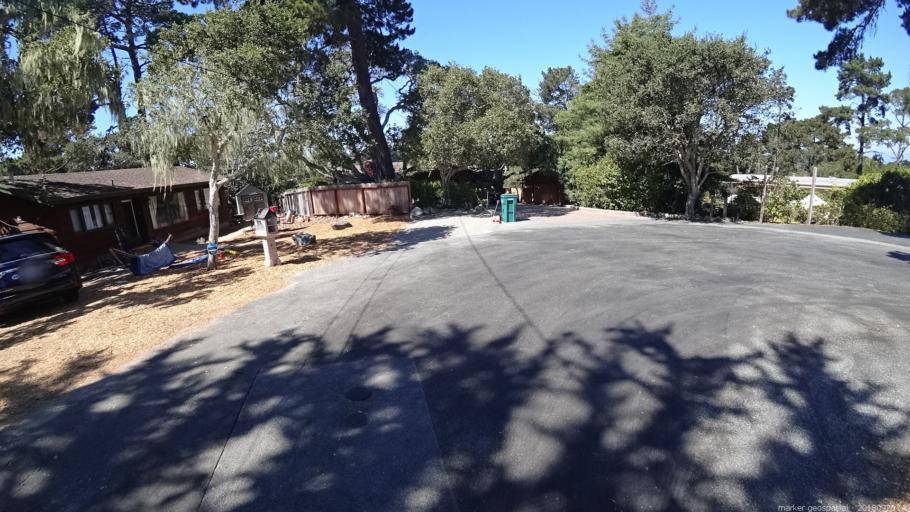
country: US
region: California
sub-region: Monterey County
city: Monterey
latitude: 36.5791
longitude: -121.8724
